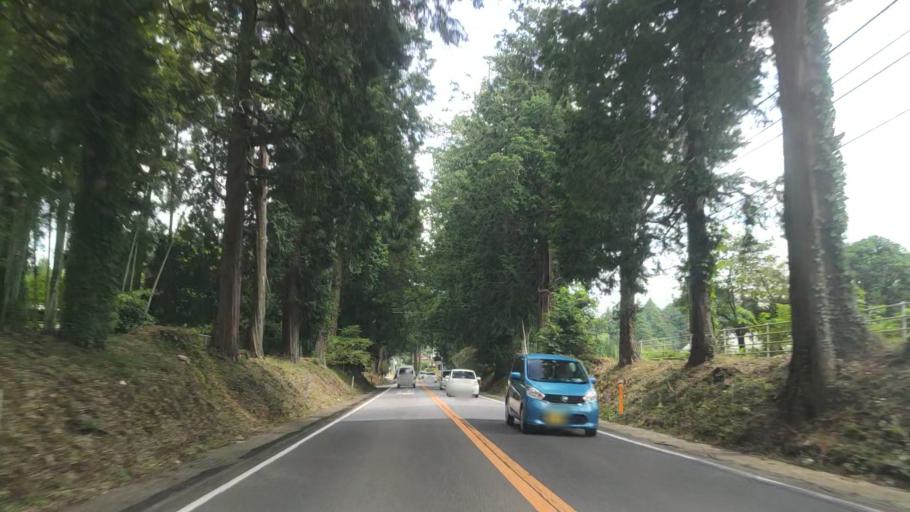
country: JP
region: Tochigi
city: Imaichi
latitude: 36.6822
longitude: 139.7906
